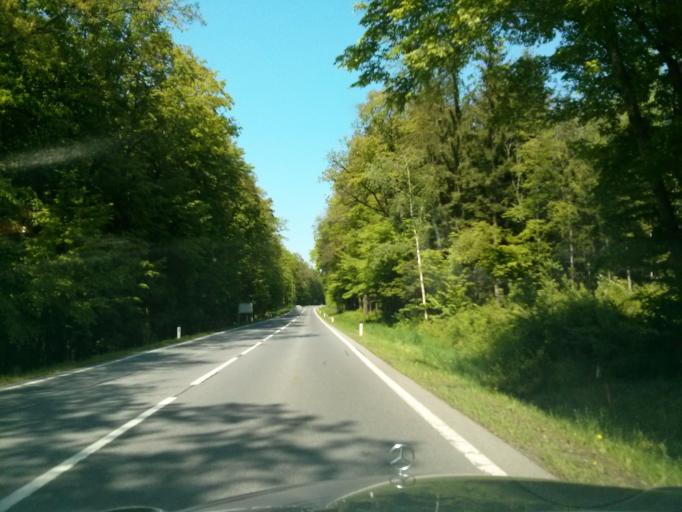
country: AT
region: Burgenland
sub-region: Politischer Bezirk Oberwart
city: Bad Tatzmannsdorf
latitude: 47.3271
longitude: 16.2193
